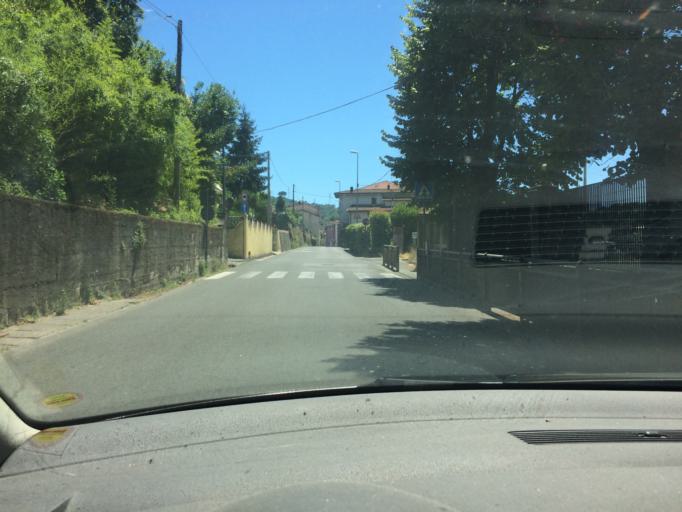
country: IT
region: Tuscany
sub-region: Provincia di Massa-Carrara
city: Carrara
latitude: 44.0634
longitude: 10.0832
